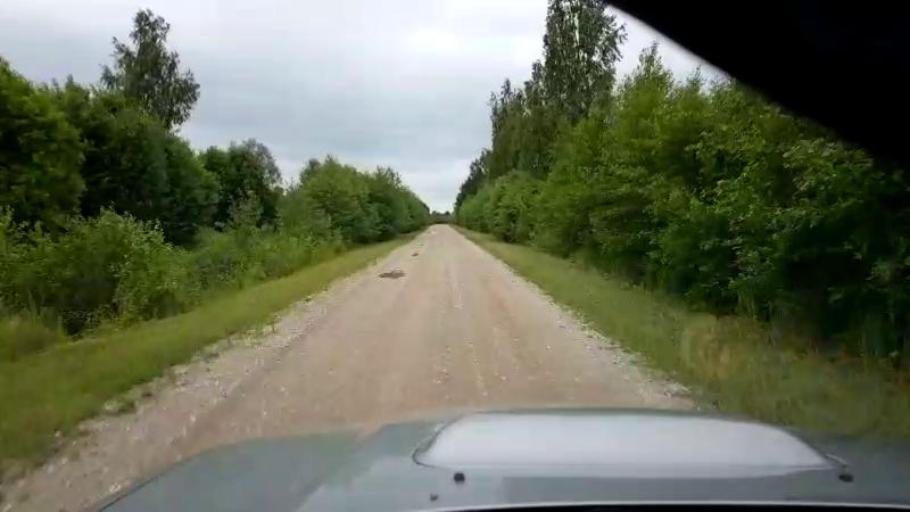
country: EE
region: Paernumaa
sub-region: Halinga vald
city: Parnu-Jaagupi
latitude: 58.5573
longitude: 24.5620
